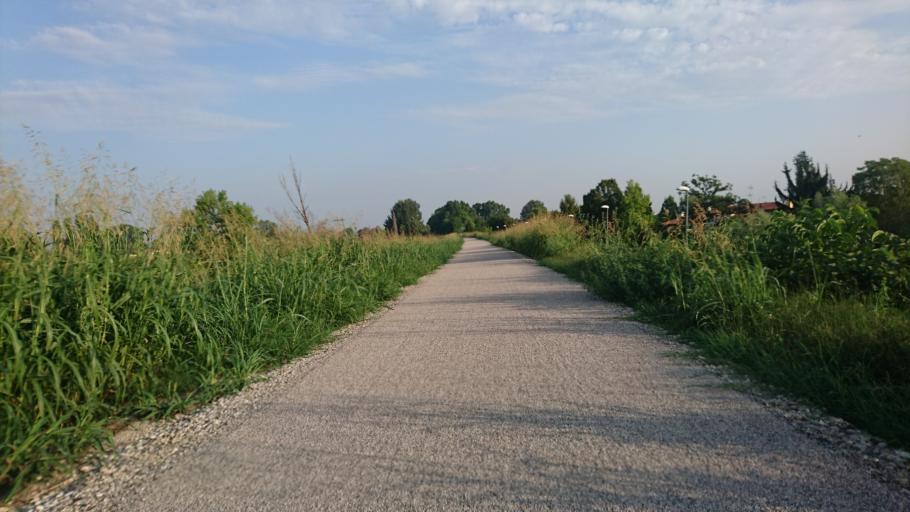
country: IT
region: Veneto
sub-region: Provincia di Padova
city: Oltre Brenta
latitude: 45.4097
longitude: 11.9973
